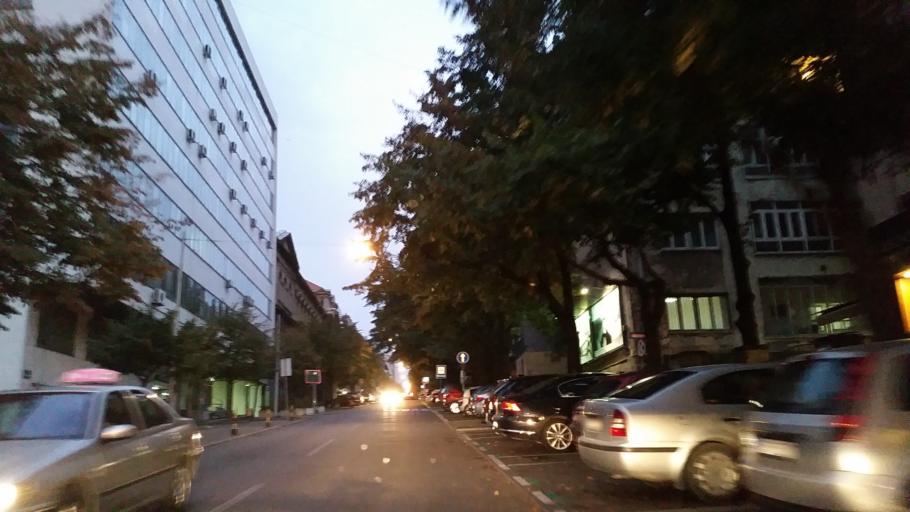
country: RS
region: Central Serbia
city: Belgrade
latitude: 44.8046
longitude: 20.4594
